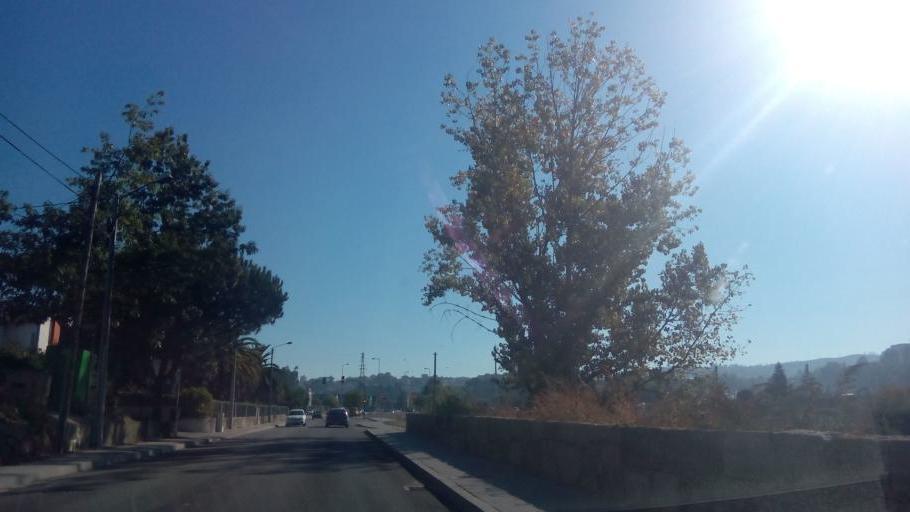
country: PT
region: Porto
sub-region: Paredes
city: Paredes
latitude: 41.2028
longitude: -8.3196
